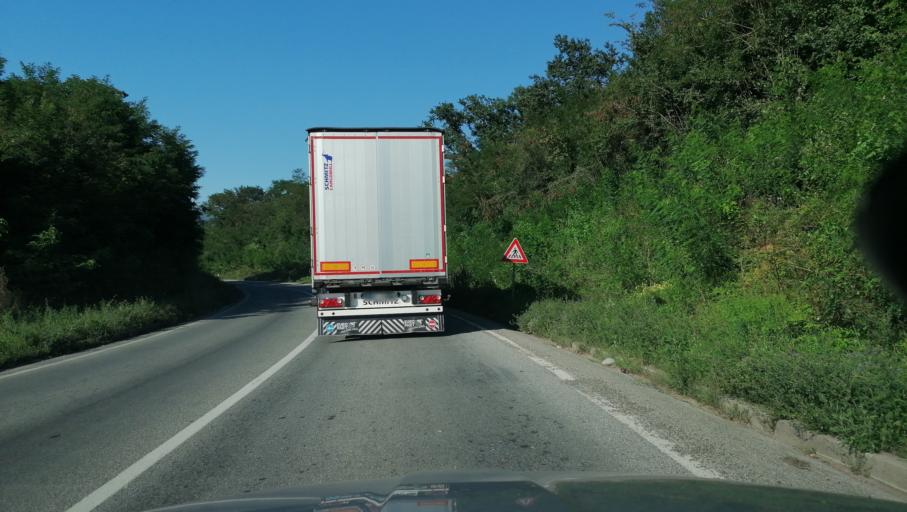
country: RS
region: Central Serbia
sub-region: Raski Okrug
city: Kraljevo
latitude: 43.7354
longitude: 20.6702
